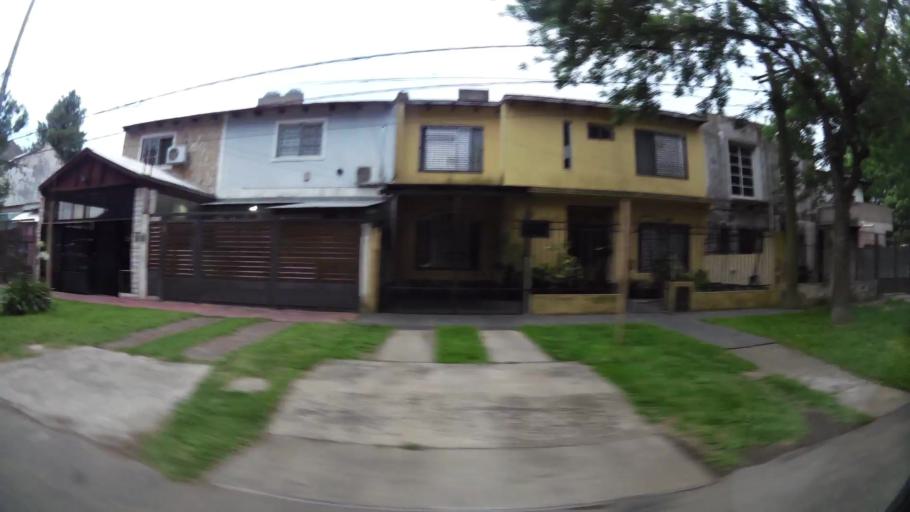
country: AR
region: Santa Fe
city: Granadero Baigorria
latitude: -32.8775
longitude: -60.7049
